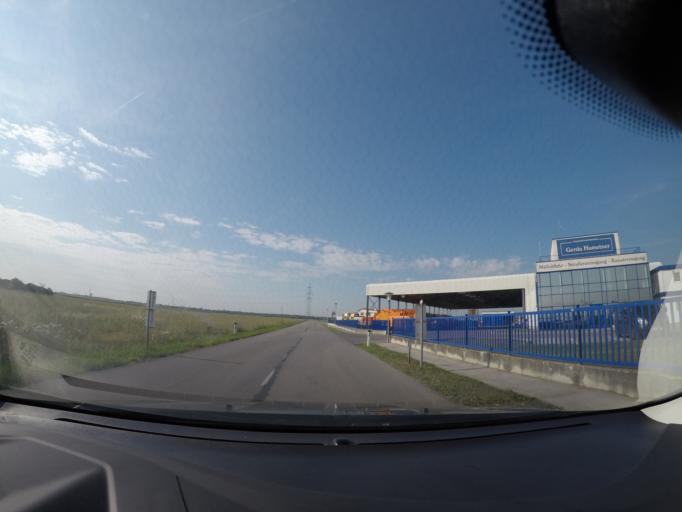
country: AT
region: Lower Austria
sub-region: Politischer Bezirk Baden
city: Teesdorf
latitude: 47.9417
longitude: 16.2895
